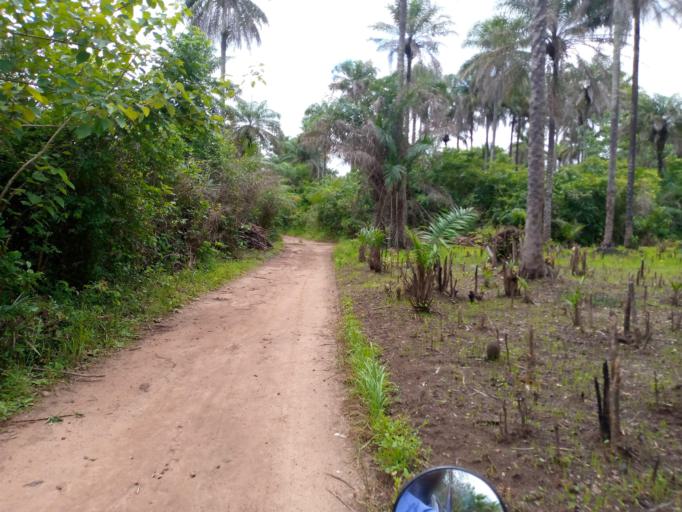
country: SL
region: Northern Province
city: Mange
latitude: 8.9745
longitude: -12.8224
